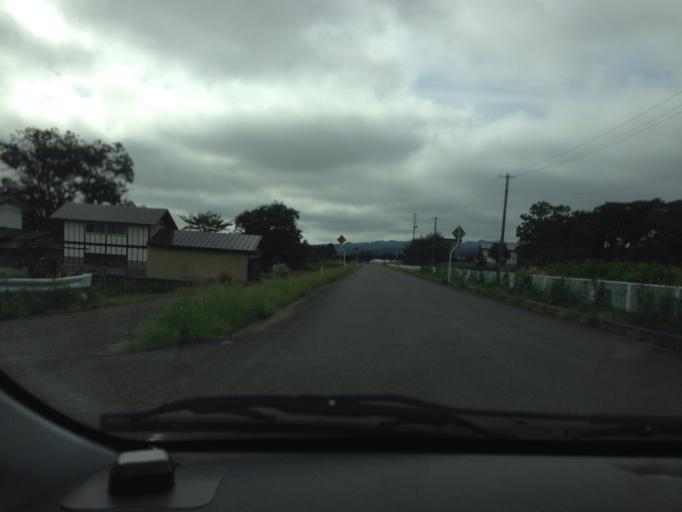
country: JP
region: Fukushima
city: Kitakata
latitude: 37.5488
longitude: 139.7992
